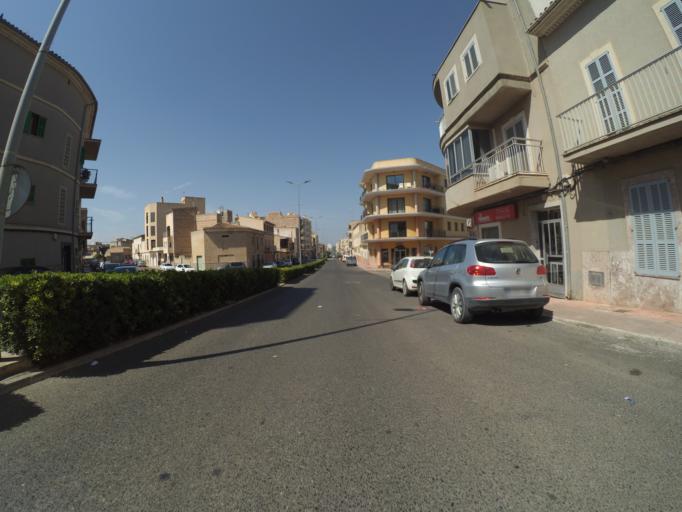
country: ES
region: Balearic Islands
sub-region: Illes Balears
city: Manacor
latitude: 39.5622
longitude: 3.2085
